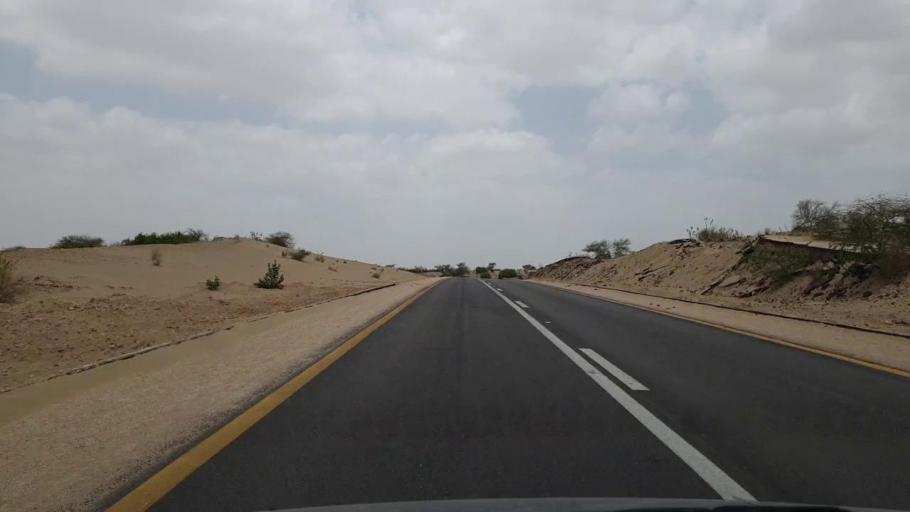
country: PK
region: Sindh
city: Naukot
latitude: 24.8425
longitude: 69.5539
